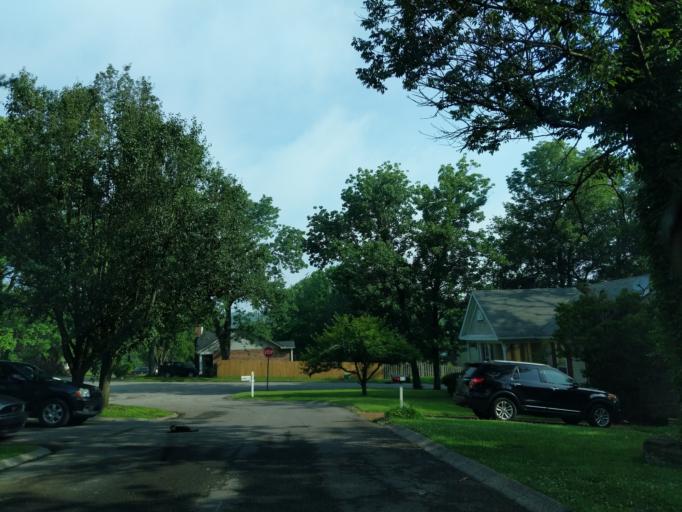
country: US
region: Tennessee
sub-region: Davidson County
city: Goodlettsville
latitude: 36.3144
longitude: -86.6901
